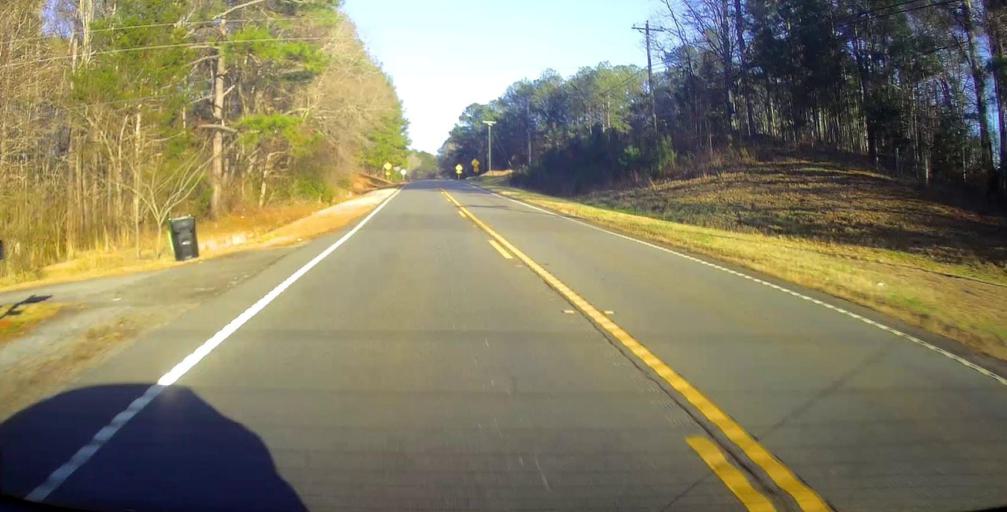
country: US
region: Georgia
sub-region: Upson County
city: Thomaston
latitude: 32.8788
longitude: -84.3741
